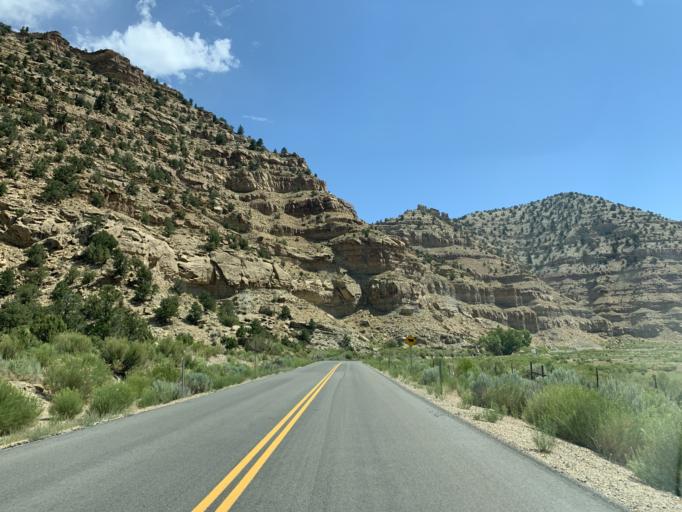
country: US
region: Utah
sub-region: Carbon County
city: East Carbon City
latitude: 39.8038
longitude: -110.3817
